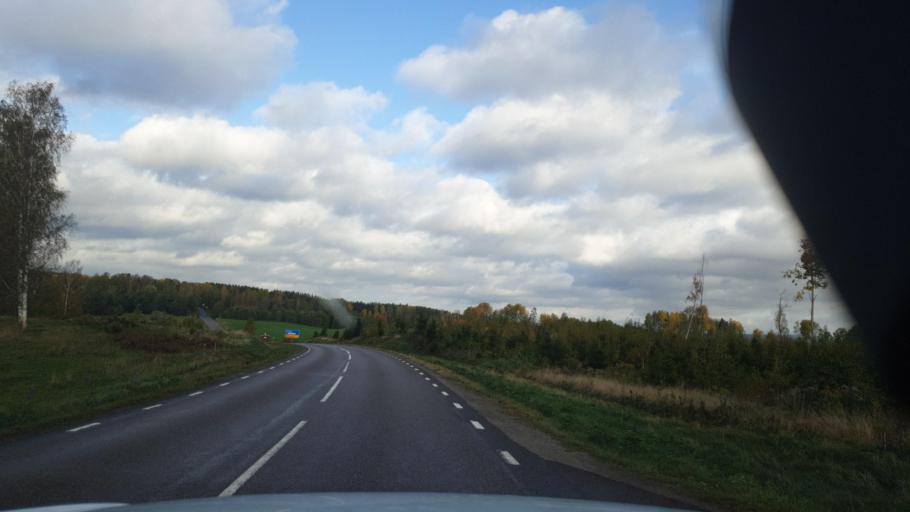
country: SE
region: Vaermland
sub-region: Arvika Kommun
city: Arvika
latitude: 59.5233
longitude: 12.6230
